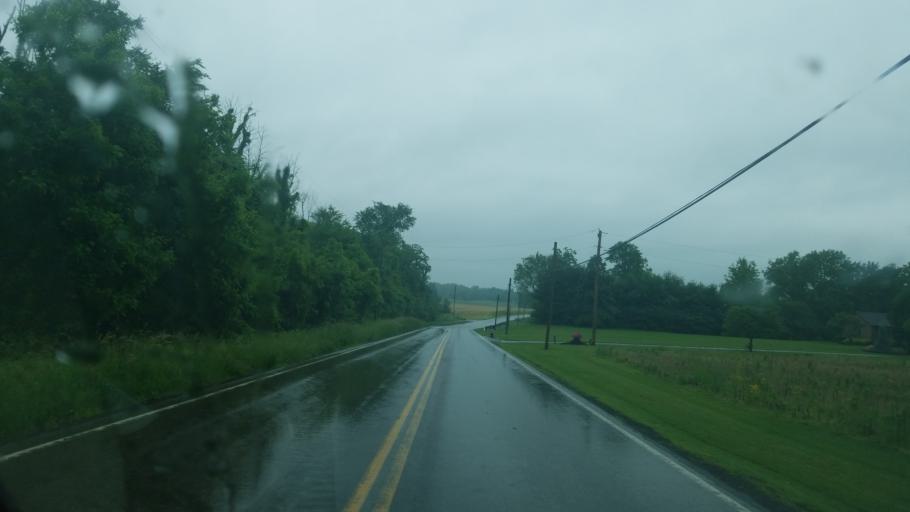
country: US
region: Ohio
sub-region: Huron County
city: Greenwich
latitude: 40.9390
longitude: -82.5496
